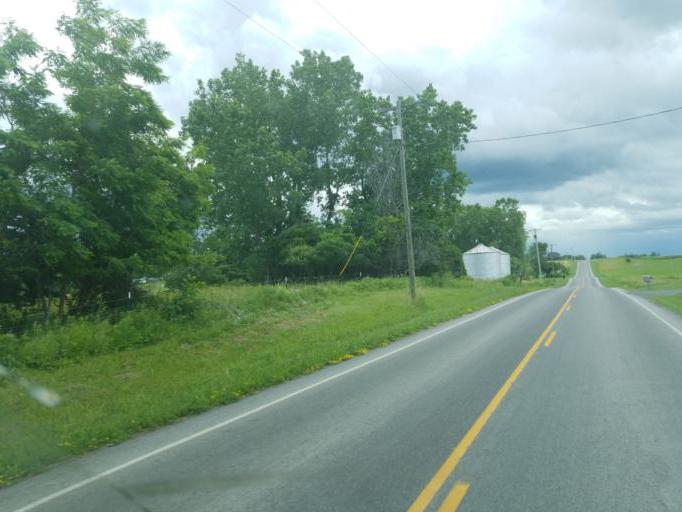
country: US
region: New York
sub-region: Wayne County
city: Lyons
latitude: 43.0249
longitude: -76.9256
